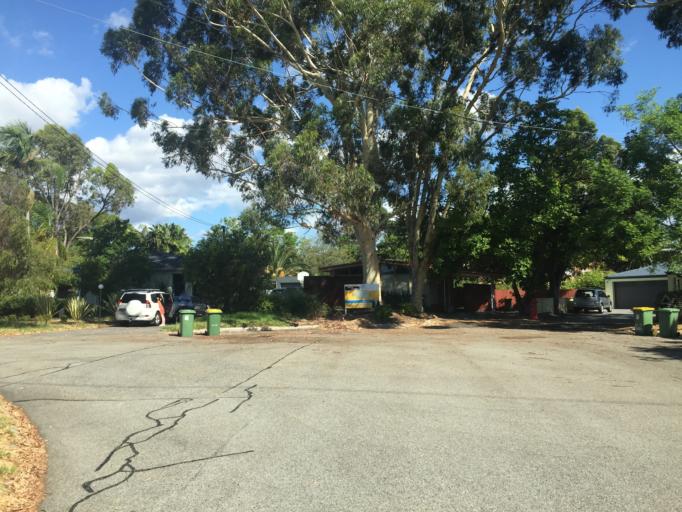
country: AU
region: Western Australia
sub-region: Belmont
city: Belmont
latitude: -31.9447
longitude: 115.9334
